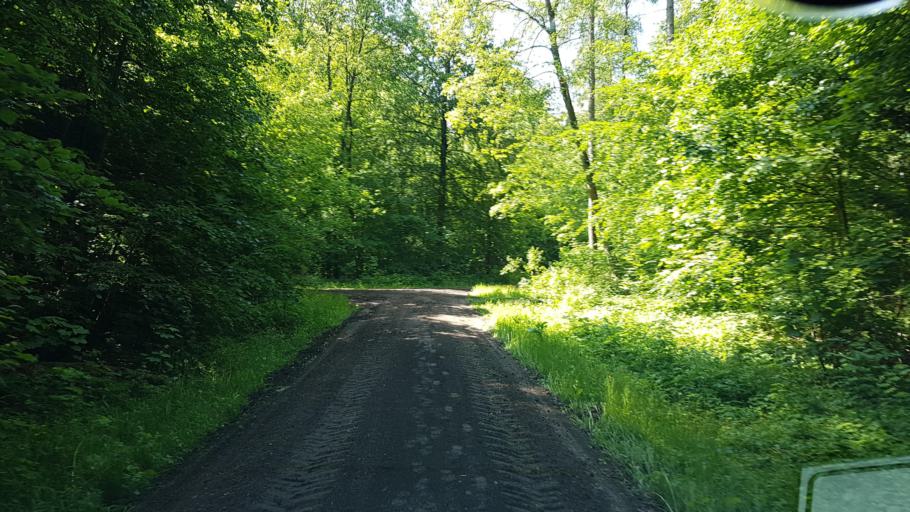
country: DE
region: Lower Saxony
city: Twieflingen
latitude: 52.1442
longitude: 10.9271
